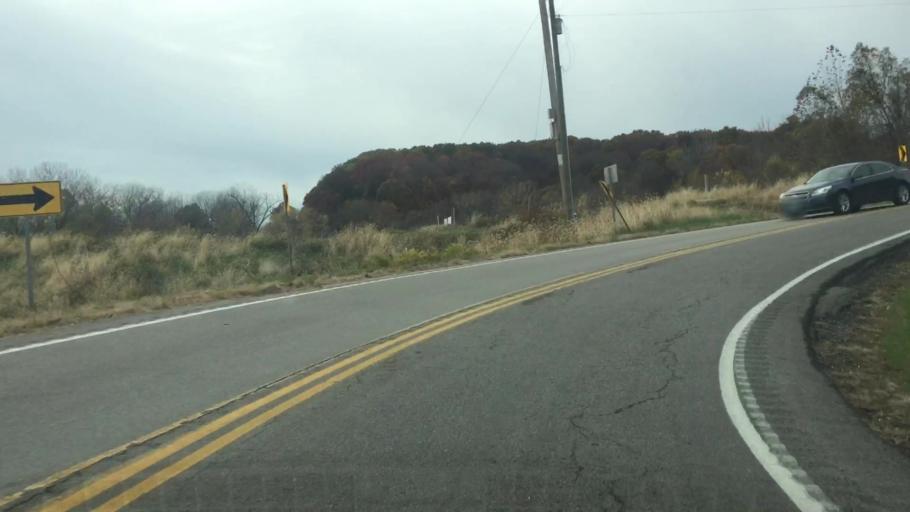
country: US
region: Missouri
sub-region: Gasconade County
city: Hermann
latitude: 38.7053
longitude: -91.6243
